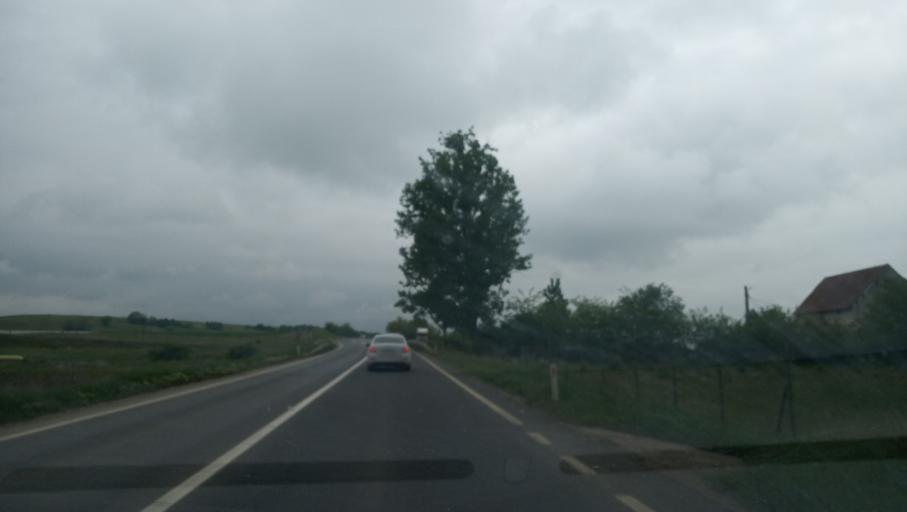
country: RO
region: Alba
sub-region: Comuna Saliste
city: Salistea
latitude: 45.9329
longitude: 23.3698
